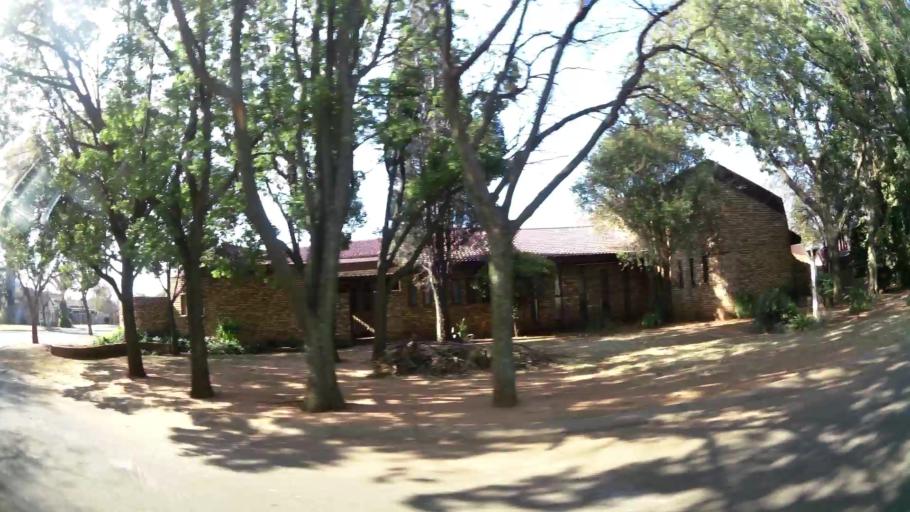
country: ZA
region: Gauteng
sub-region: West Rand District Municipality
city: Randfontein
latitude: -26.1787
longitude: 27.6886
